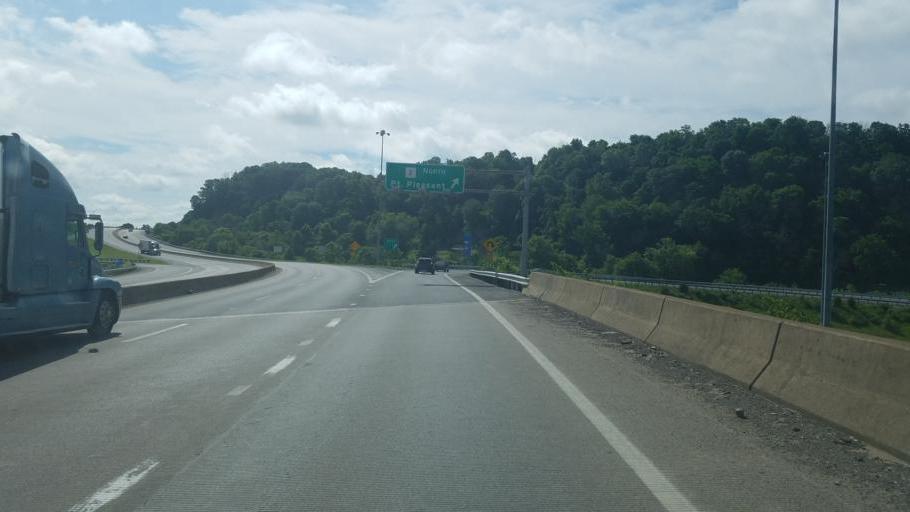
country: US
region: West Virginia
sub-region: Mason County
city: Point Pleasant
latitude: 38.8311
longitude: -82.1426
